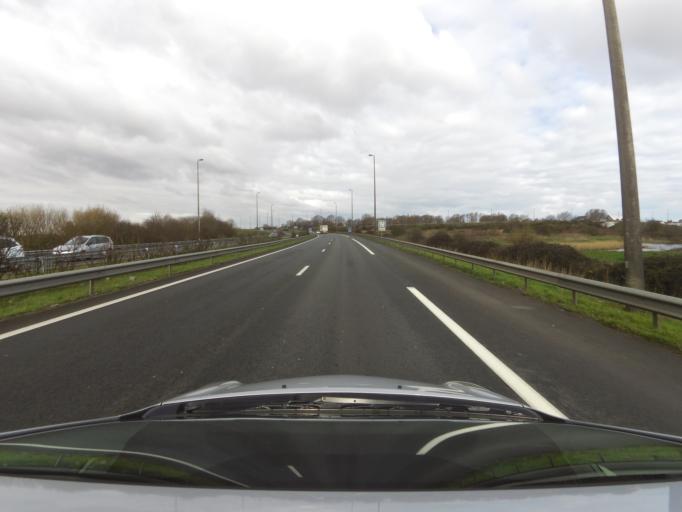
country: FR
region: Nord-Pas-de-Calais
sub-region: Departement du Pas-de-Calais
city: Coulogne
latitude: 50.9353
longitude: 1.8800
